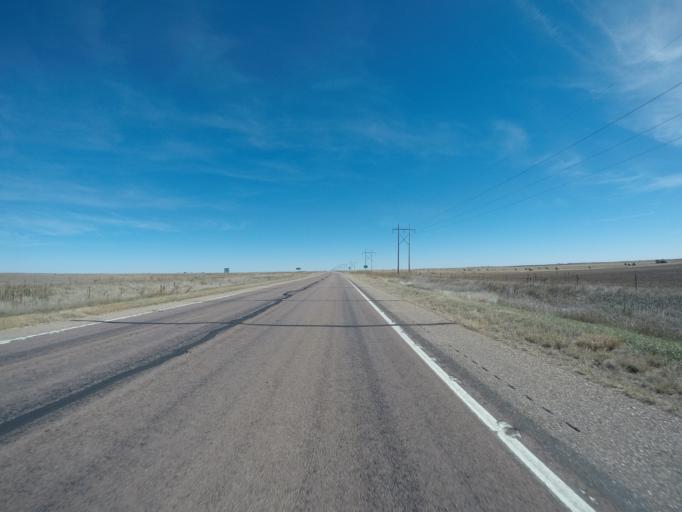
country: US
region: Colorado
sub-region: Yuma County
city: Yuma
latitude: 39.6548
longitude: -102.8035
